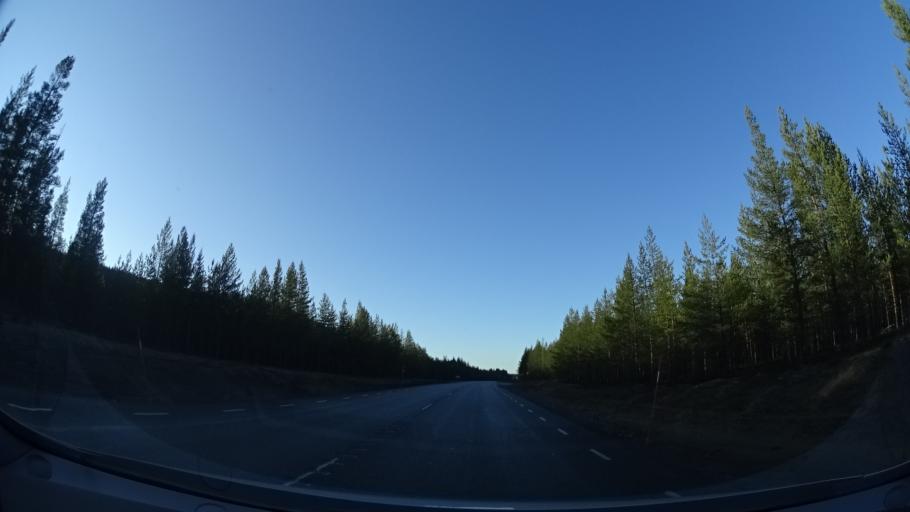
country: SE
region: Vaesterbotten
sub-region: Skelleftea Kommun
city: Langsele
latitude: 64.9209
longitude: 20.0625
